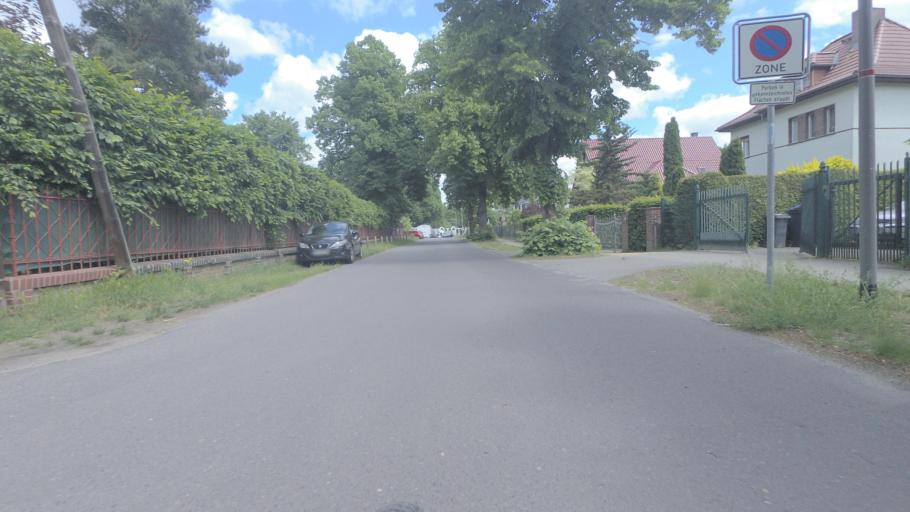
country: DE
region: Brandenburg
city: Falkensee
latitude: 52.5716
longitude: 13.1202
